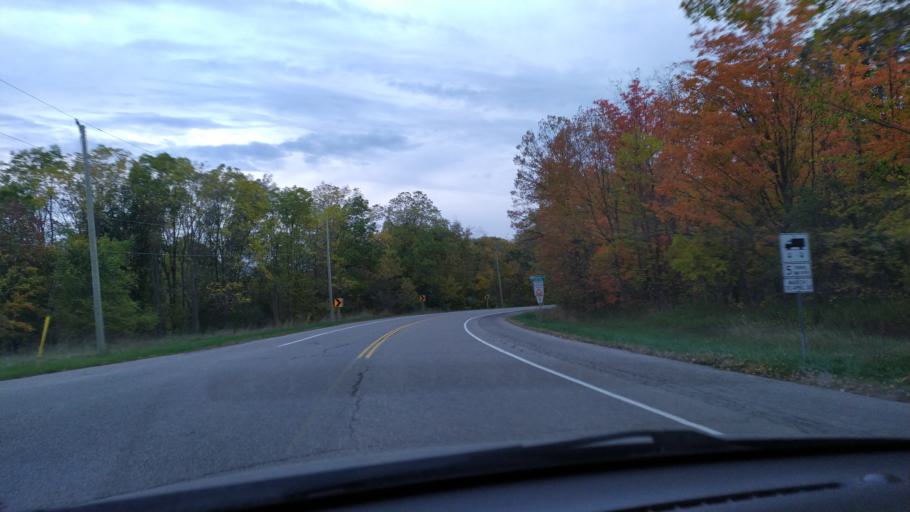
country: CA
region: Ontario
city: Stratford
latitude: 43.4683
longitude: -80.7945
